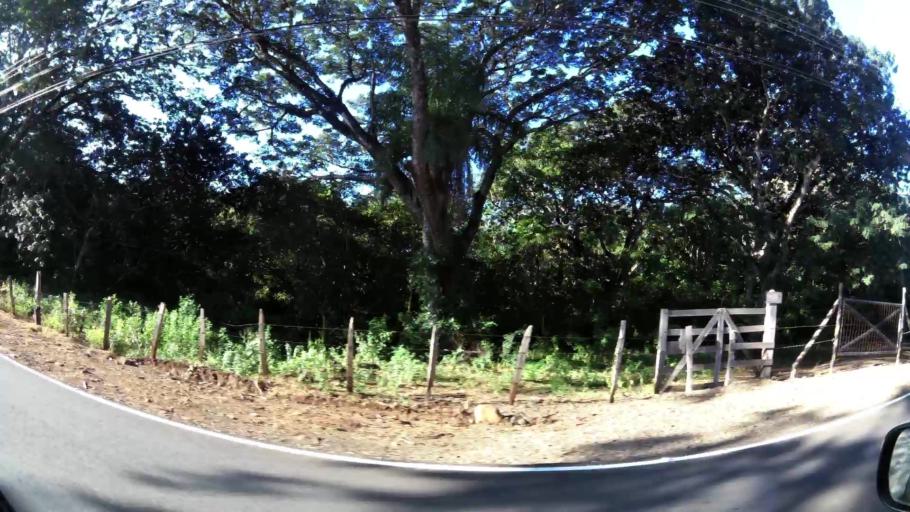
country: CR
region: Puntarenas
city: Miramar
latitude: 10.1439
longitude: -84.8489
